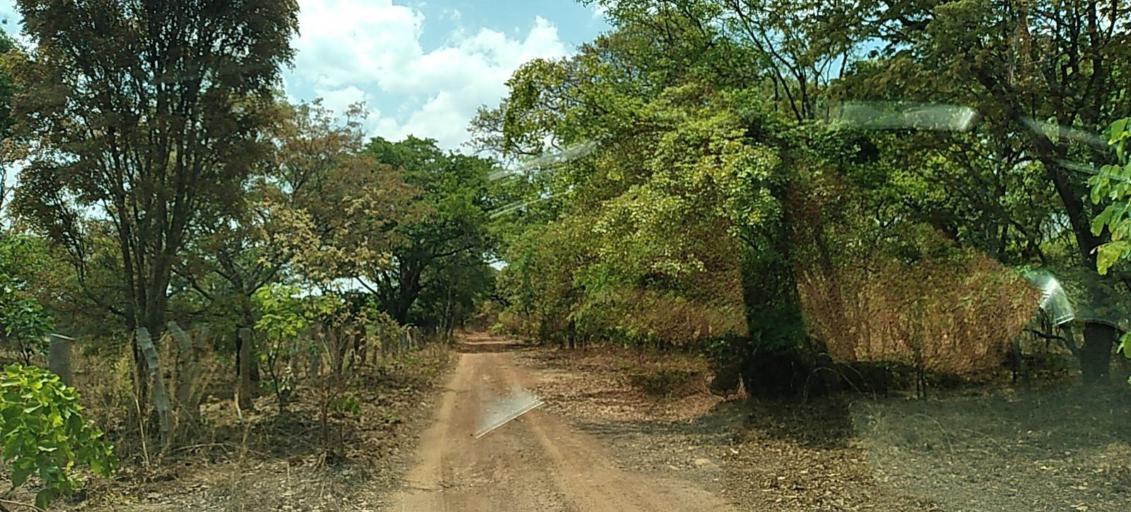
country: ZM
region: Copperbelt
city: Chililabombwe
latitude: -12.4609
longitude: 27.6461
